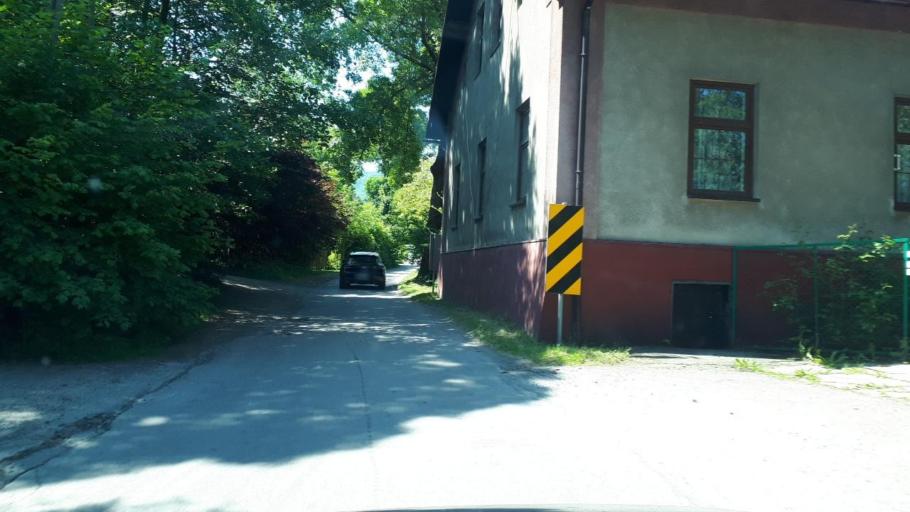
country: PL
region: Silesian Voivodeship
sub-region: Powiat bielski
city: Jaworze
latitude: 49.7900
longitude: 18.9456
